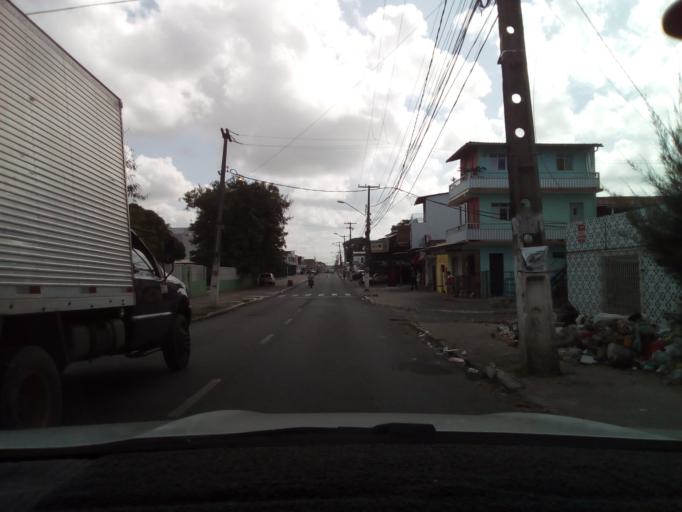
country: BR
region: Paraiba
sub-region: Bayeux
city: Bayeux
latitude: -7.1235
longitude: -34.9191
